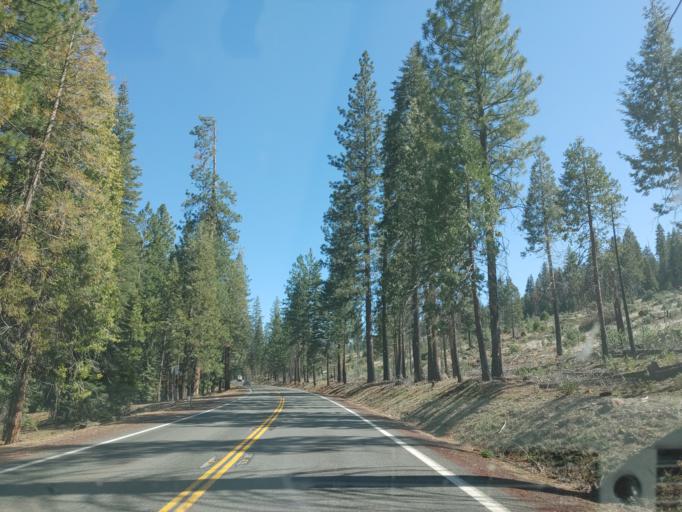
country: US
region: California
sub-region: Shasta County
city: Burney
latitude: 40.7587
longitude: -121.4977
